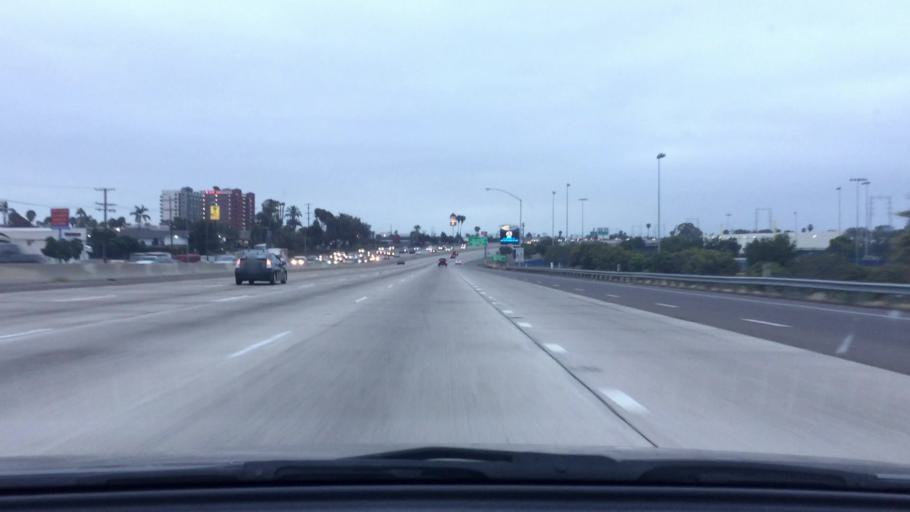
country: US
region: California
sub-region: San Diego County
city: National City
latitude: 32.6807
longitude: -117.1107
